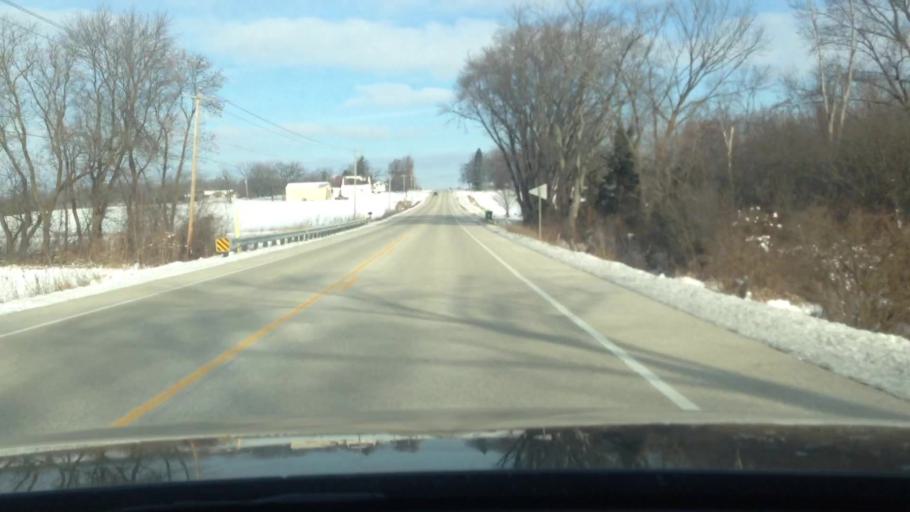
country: US
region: Wisconsin
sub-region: Walworth County
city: East Troy
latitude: 42.7088
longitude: -88.4052
